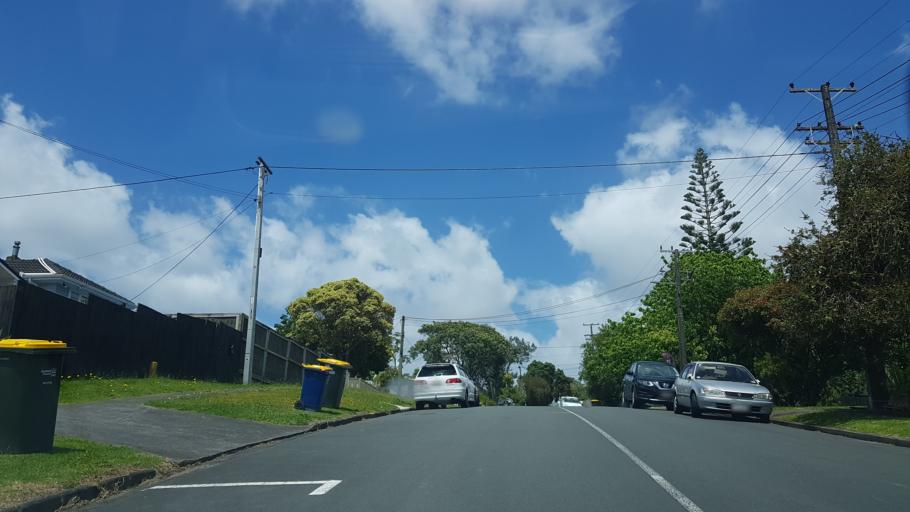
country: NZ
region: Auckland
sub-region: Auckland
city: North Shore
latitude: -36.8035
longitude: 174.7129
